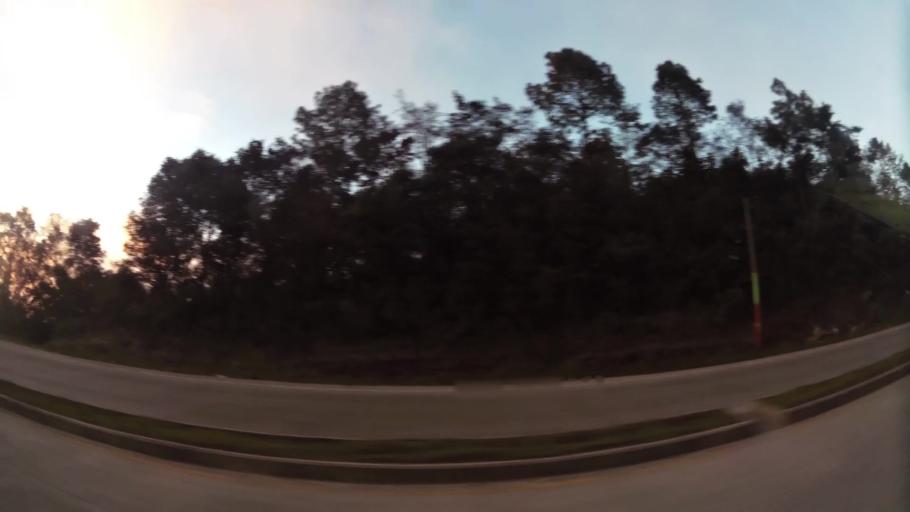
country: GT
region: Solola
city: Concepcion
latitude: 14.8359
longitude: -91.1100
